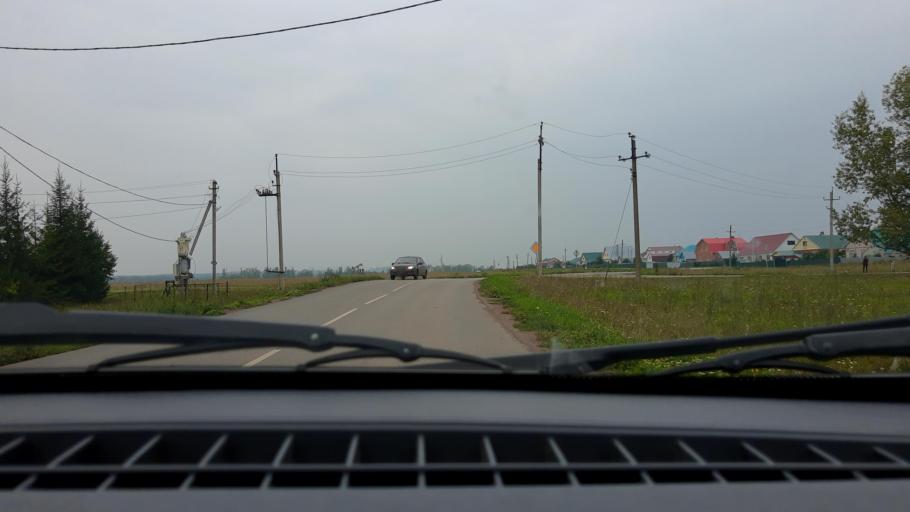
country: RU
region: Bashkortostan
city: Mikhaylovka
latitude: 54.8064
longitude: 55.7893
